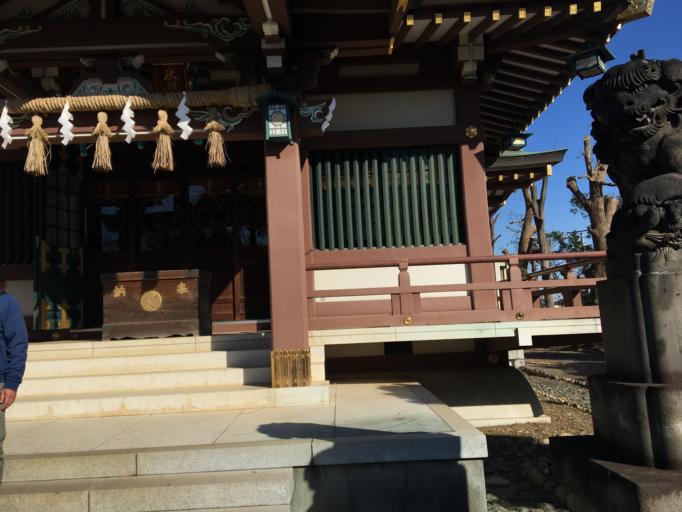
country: JP
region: Saitama
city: Wako
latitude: 35.7853
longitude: 139.6400
